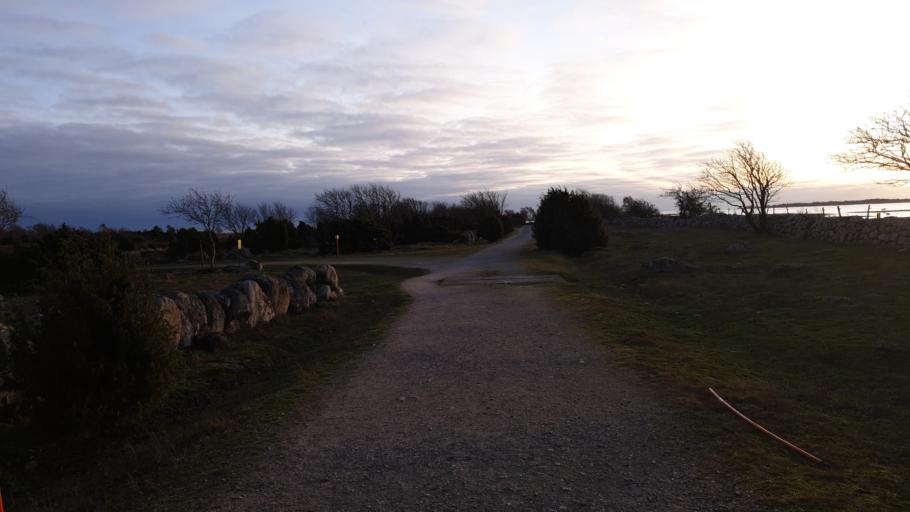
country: SE
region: Blekinge
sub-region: Karlskrona Kommun
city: Jaemjoe
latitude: 56.0801
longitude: 15.8415
